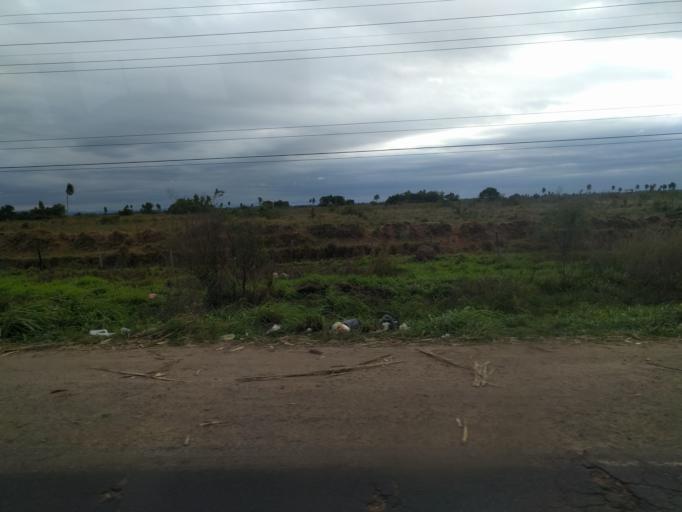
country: BO
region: Santa Cruz
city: La Belgica
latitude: -17.6224
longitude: -63.1589
